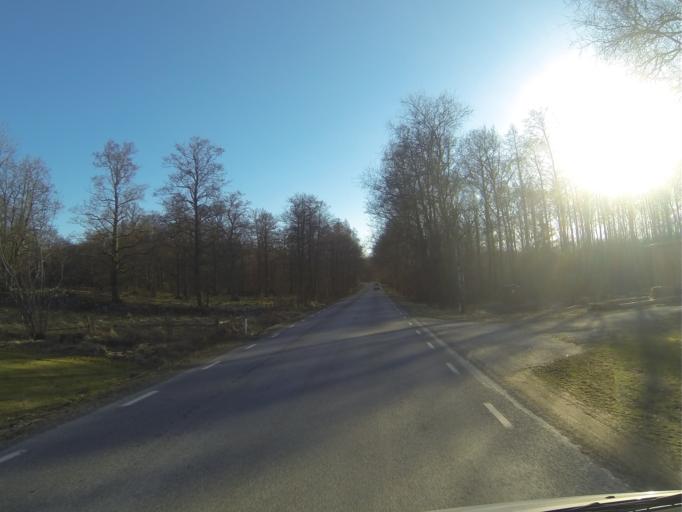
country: SE
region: Skane
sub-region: Horby Kommun
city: Hoerby
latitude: 55.8895
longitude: 13.6667
